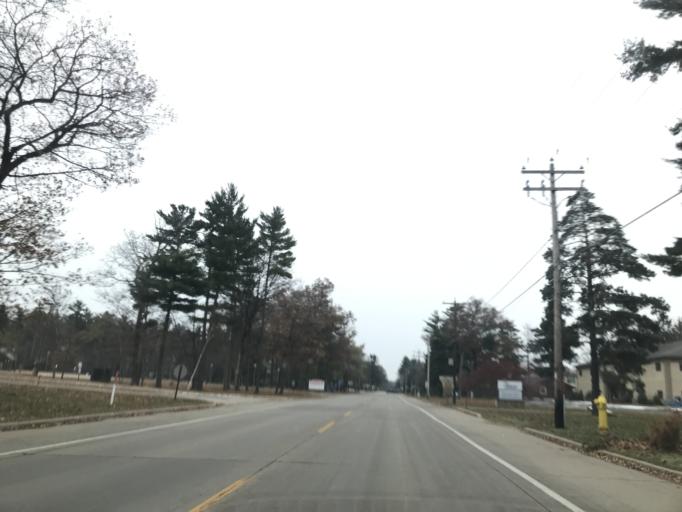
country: US
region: Wisconsin
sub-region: Marinette County
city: Marinette
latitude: 45.0726
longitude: -87.6194
